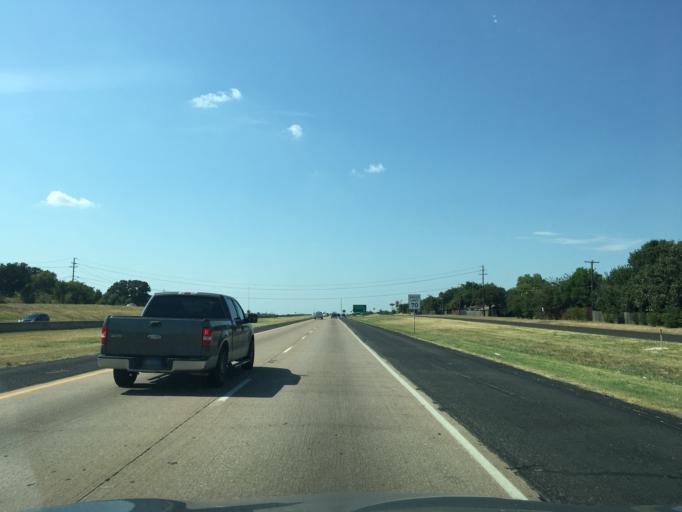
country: US
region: Texas
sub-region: Tarrant County
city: Kennedale
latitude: 32.6405
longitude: -97.1811
